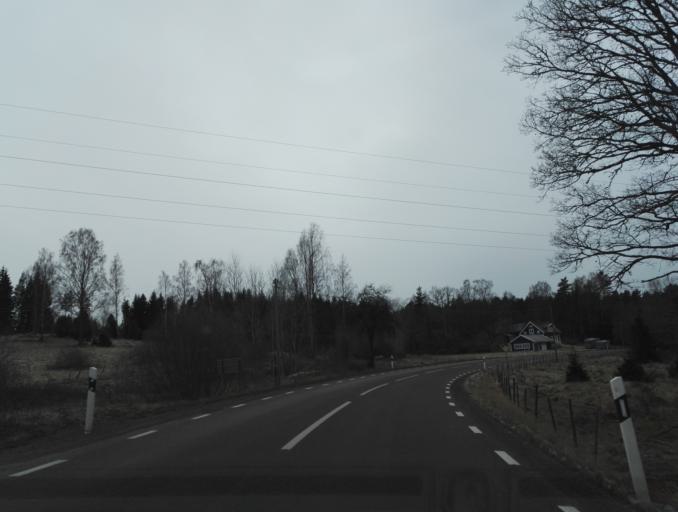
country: SE
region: Kalmar
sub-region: Hultsfreds Kommun
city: Virserum
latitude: 57.3347
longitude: 15.6010
